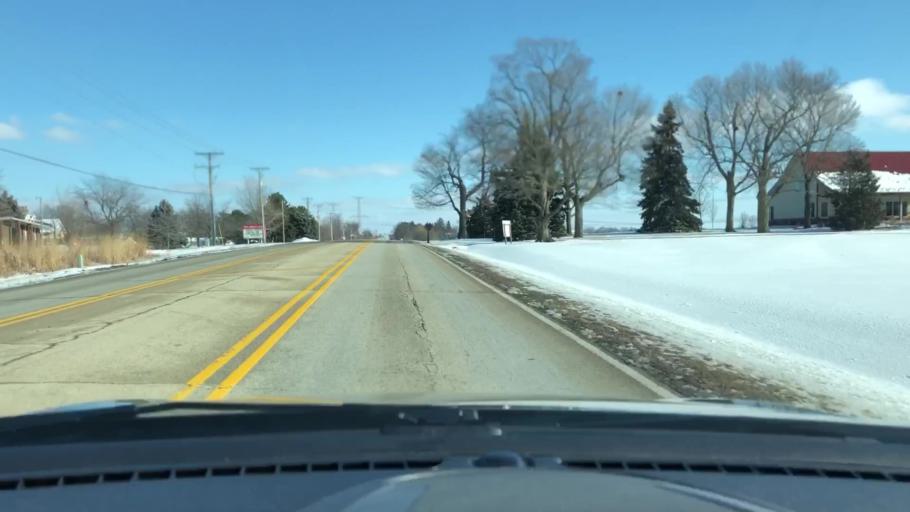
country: US
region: Illinois
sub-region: Will County
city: Ingalls Park
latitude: 41.4816
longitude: -88.0401
